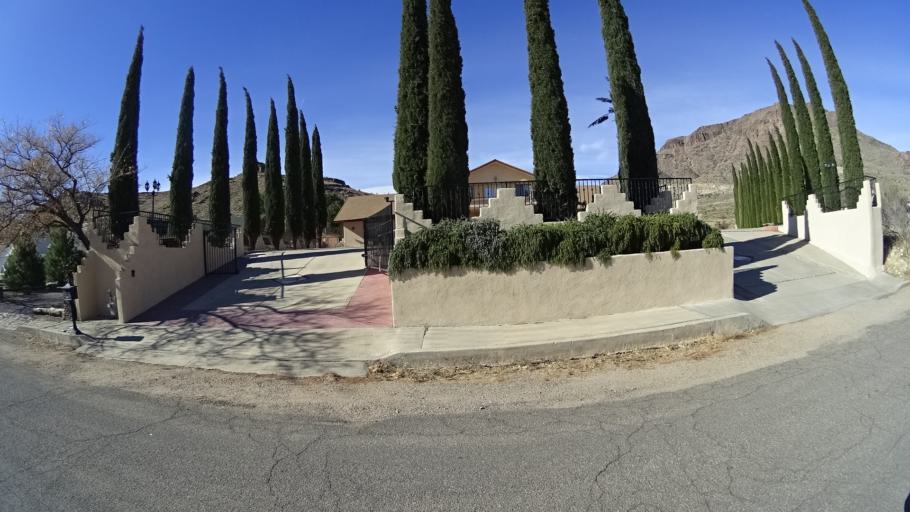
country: US
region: Arizona
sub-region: Mohave County
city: New Kingman-Butler
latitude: 35.2685
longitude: -114.0491
